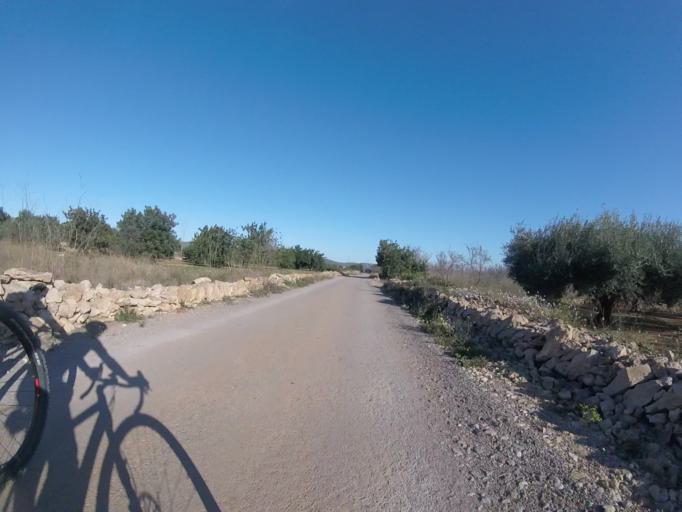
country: ES
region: Valencia
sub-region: Provincia de Castello
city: Alcala de Xivert
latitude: 40.2838
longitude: 0.2117
